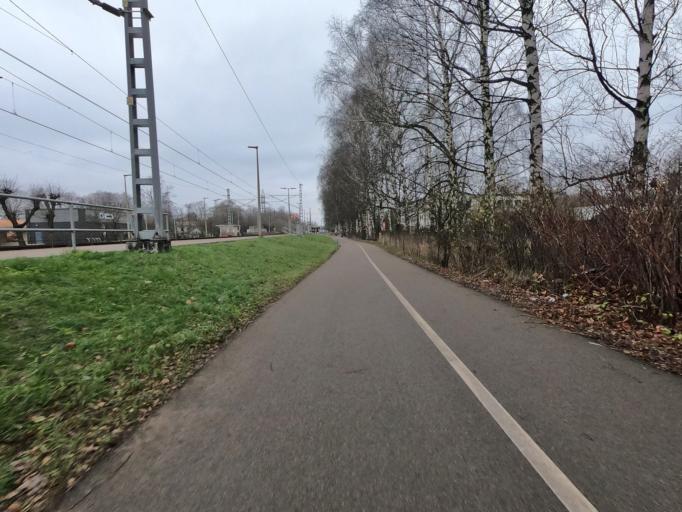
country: LV
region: Marupe
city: Marupe
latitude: 56.9504
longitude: 24.0014
